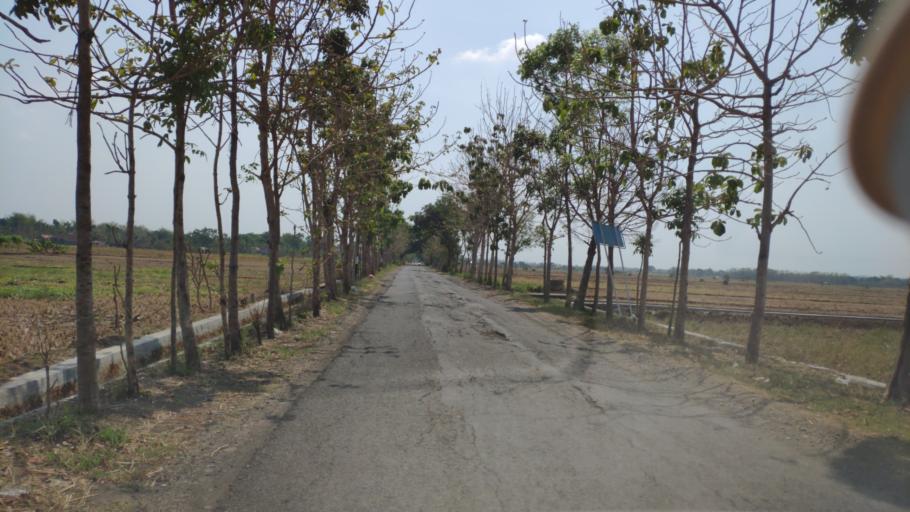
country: ID
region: Central Java
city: Kedungjenar
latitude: -6.9801
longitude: 111.4249
